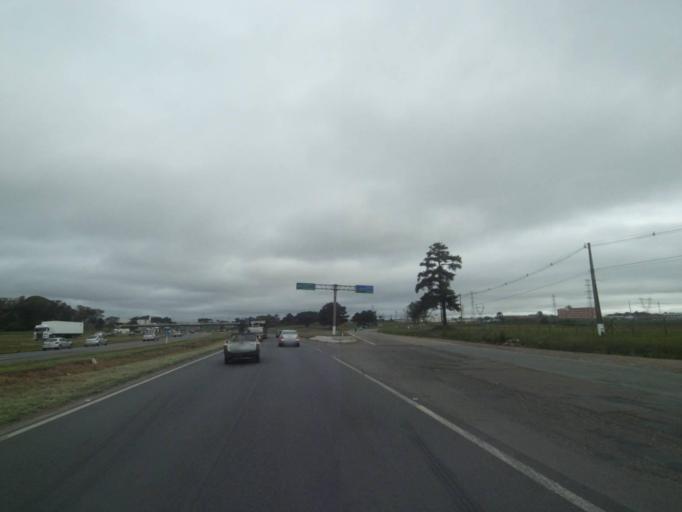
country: BR
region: Parana
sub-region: Sao Jose Dos Pinhais
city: Sao Jose dos Pinhais
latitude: -25.5434
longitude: -49.3080
